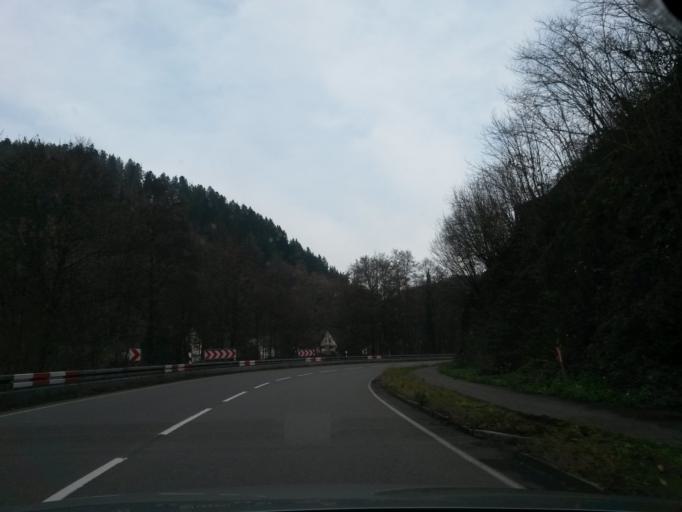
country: DE
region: Baden-Wuerttemberg
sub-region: Karlsruhe Region
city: Alpirsbach
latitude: 48.3261
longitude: 8.3946
